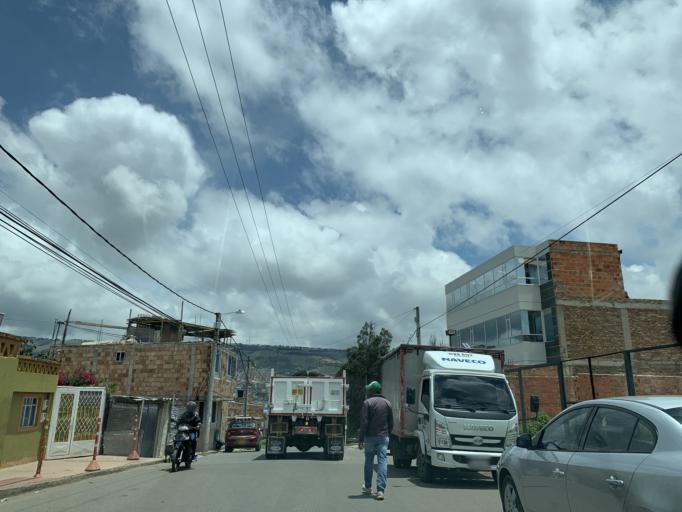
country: CO
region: Boyaca
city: Tunja
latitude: 5.5186
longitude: -73.3538
